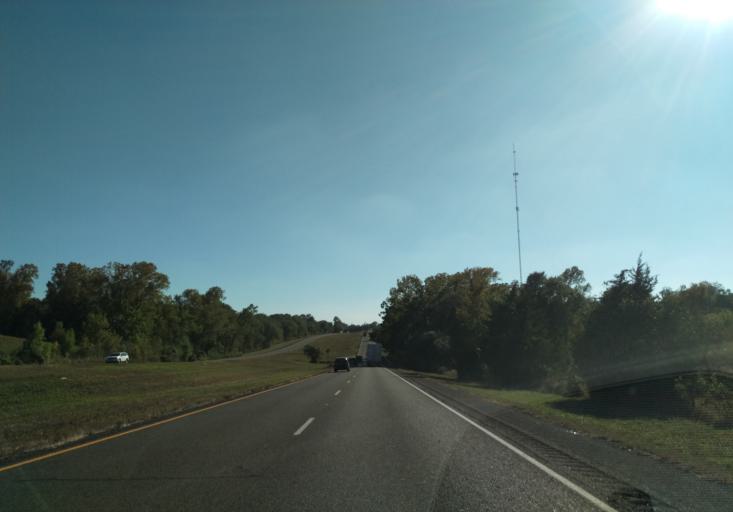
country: US
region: Texas
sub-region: Grimes County
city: Navasota
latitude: 30.2533
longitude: -96.0451
